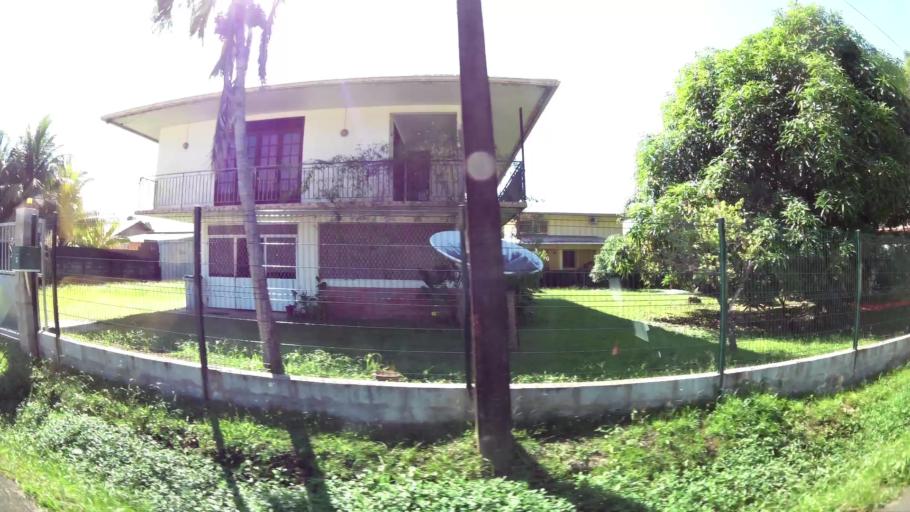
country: GF
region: Guyane
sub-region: Guyane
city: Remire-Montjoly
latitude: 4.9141
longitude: -52.2726
